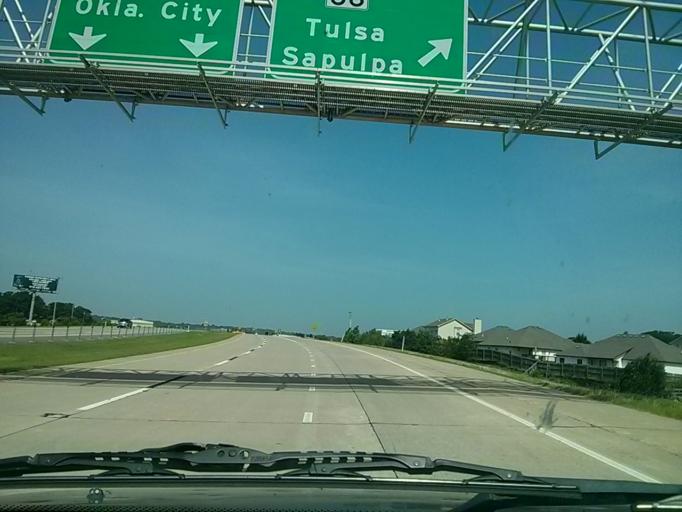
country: US
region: Oklahoma
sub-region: Creek County
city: Sapulpa
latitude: 36.0282
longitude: -96.0806
